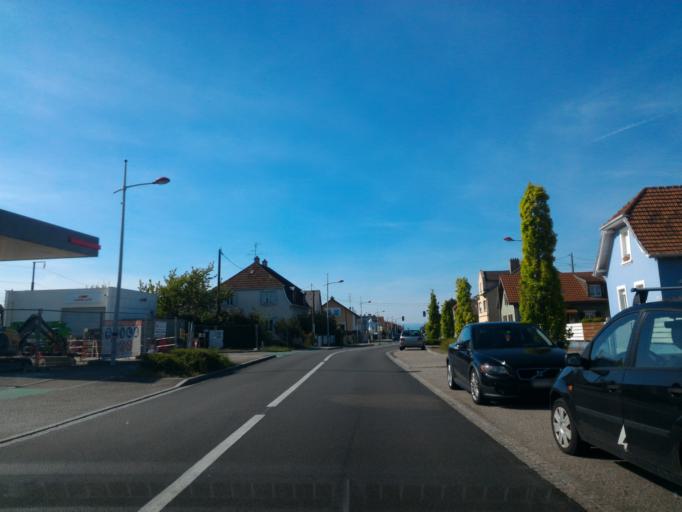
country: FR
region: Alsace
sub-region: Departement du Haut-Rhin
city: Rixheim
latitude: 47.7456
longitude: 7.4117
